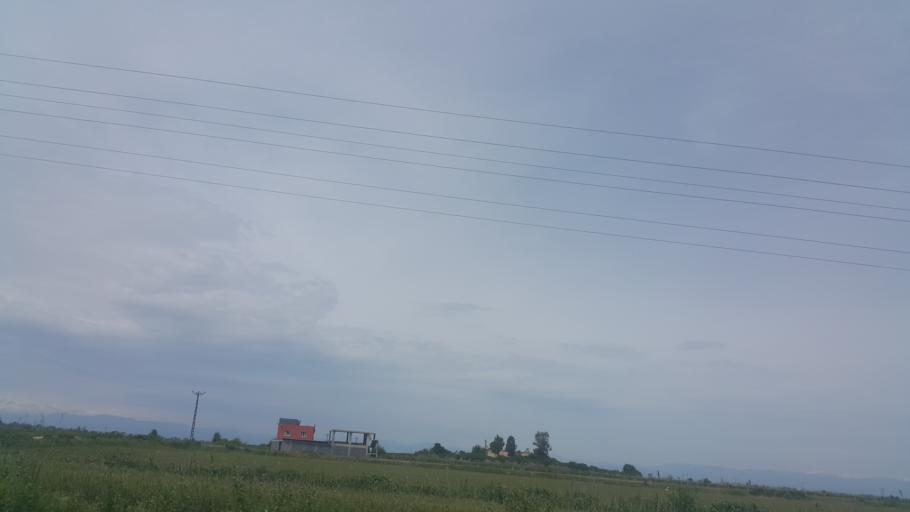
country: TR
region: Adana
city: Ceyhan
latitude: 37.0577
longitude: 35.8905
